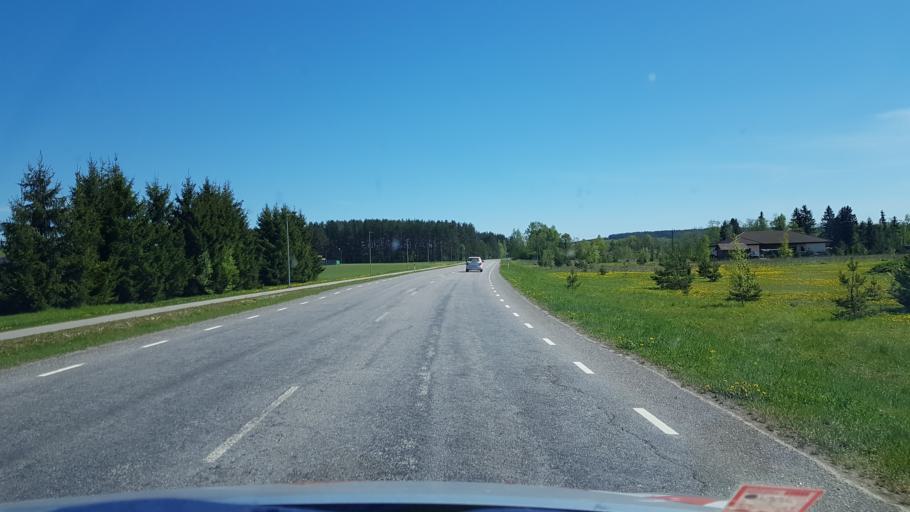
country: EE
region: Tartu
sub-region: UElenurme vald
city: Ulenurme
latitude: 58.3056
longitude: 26.8579
